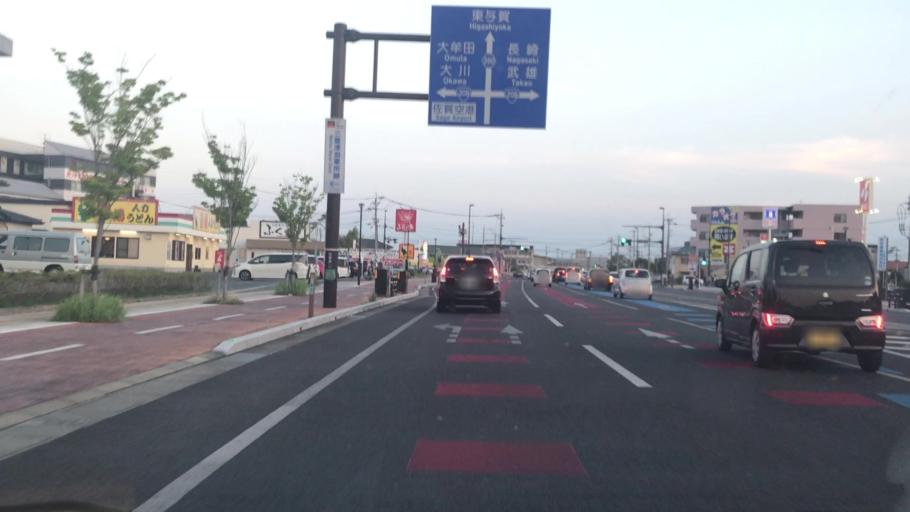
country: JP
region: Saga Prefecture
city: Saga-shi
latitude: 33.2406
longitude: 130.2944
